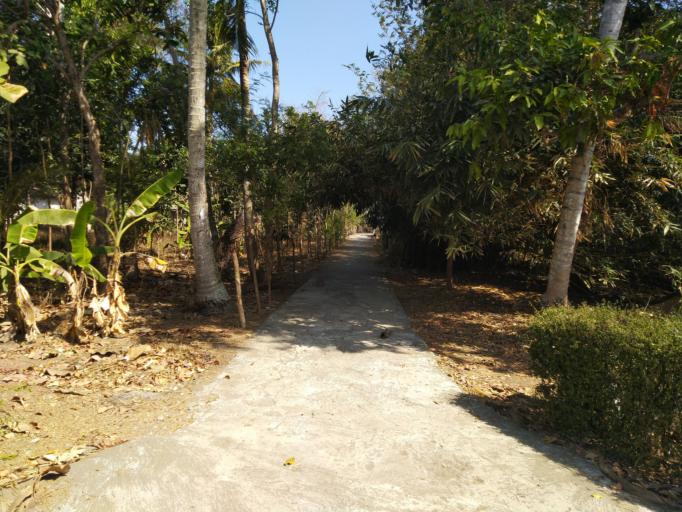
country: ID
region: Daerah Istimewa Yogyakarta
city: Bambanglipuro
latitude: -7.9967
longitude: 110.2774
